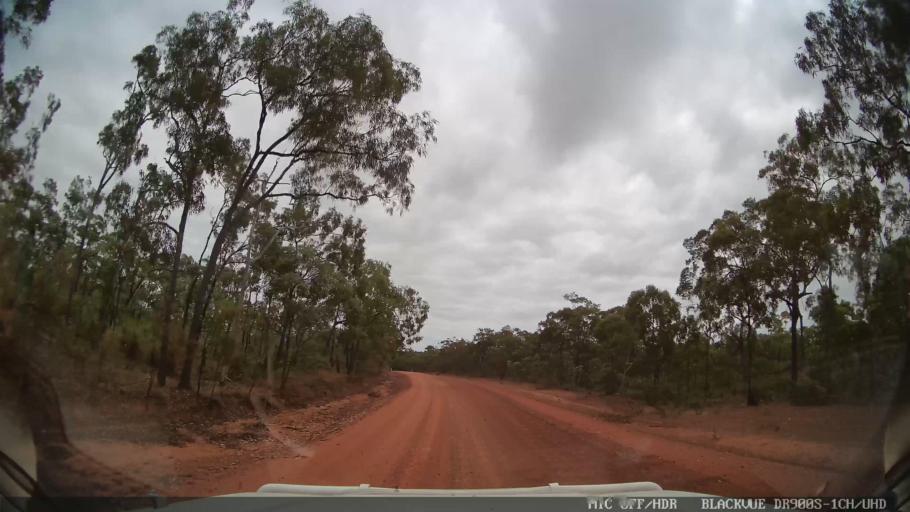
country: AU
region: Queensland
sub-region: Cook
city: Cooktown
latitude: -15.2639
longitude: 144.9548
